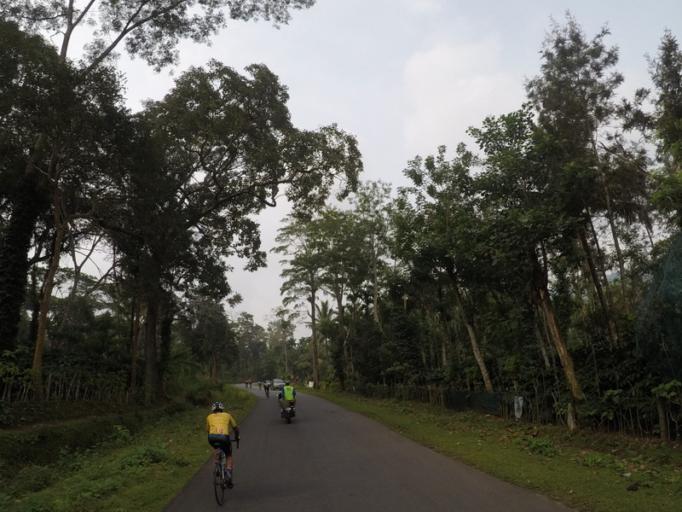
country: IN
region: Karnataka
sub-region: Chikmagalur
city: Mudigere
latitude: 13.3031
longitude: 75.4858
